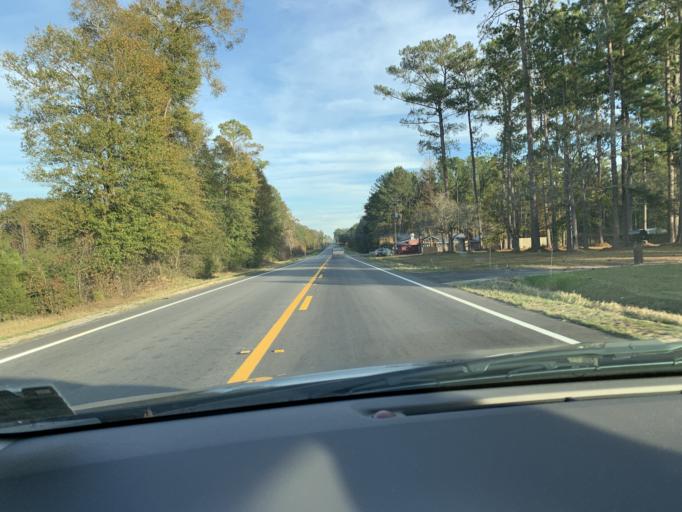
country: US
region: Georgia
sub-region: Irwin County
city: Ocilla
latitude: 31.5960
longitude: -83.1754
